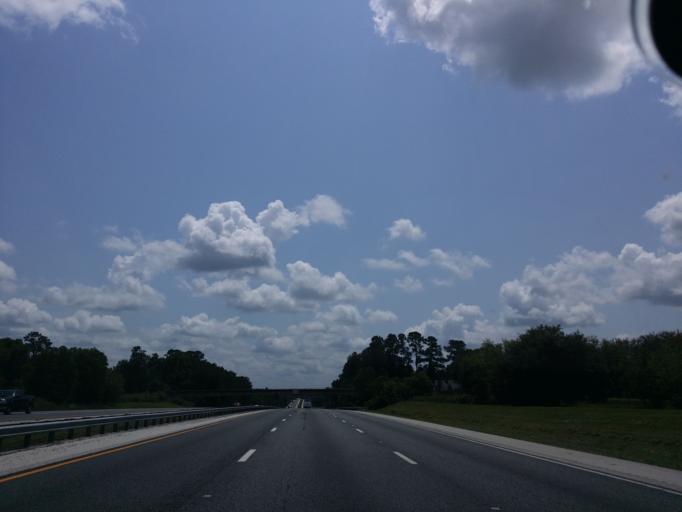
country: US
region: Florida
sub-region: Marion County
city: Citra
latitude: 29.4479
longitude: -82.2676
